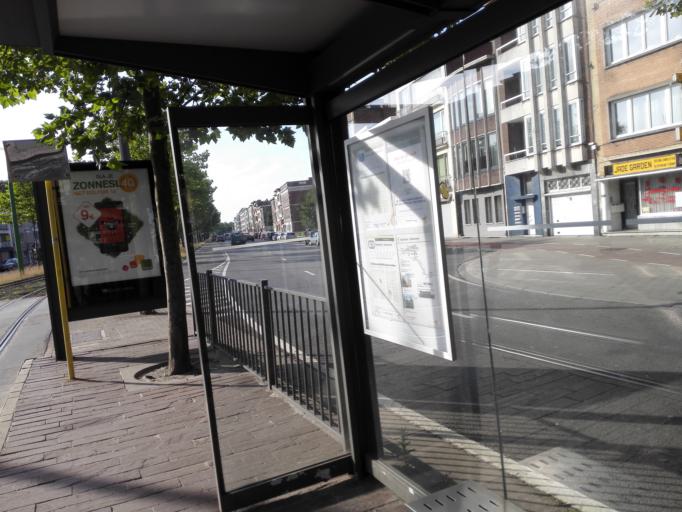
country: BE
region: Flanders
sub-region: Provincie Antwerpen
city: Mortsel
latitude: 51.1769
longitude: 4.4362
